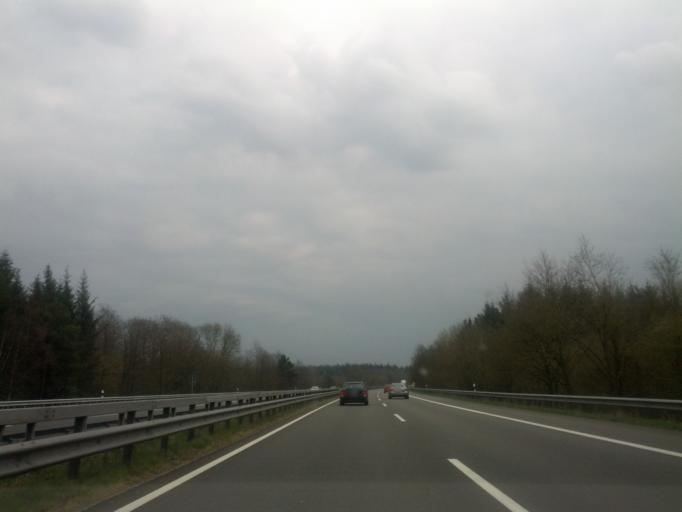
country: DE
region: Lower Saxony
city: Bad Zwischenahn
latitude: 53.2459
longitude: 8.0131
